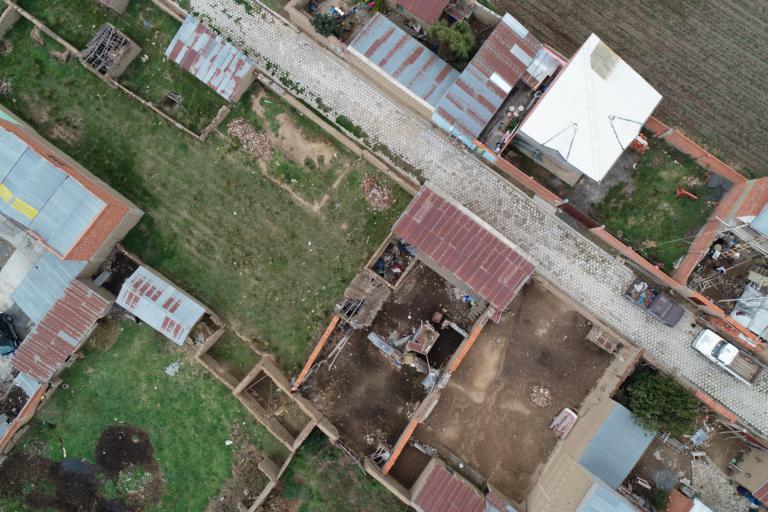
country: BO
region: La Paz
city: Huarina
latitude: -16.1885
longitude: -68.6026
